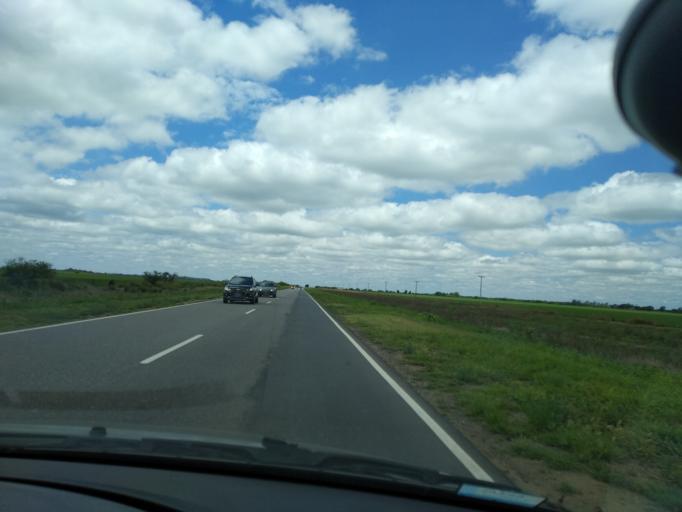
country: AR
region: Cordoba
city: Toledo
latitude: -31.6451
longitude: -64.0110
